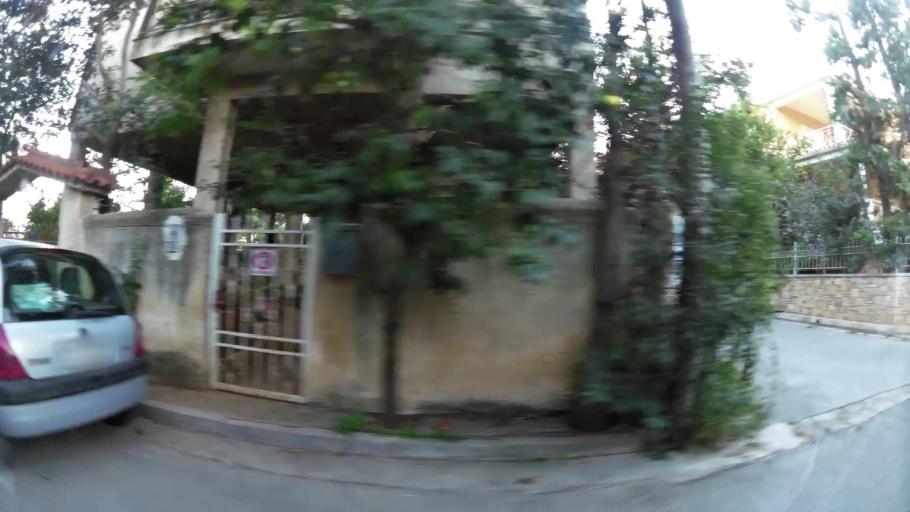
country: GR
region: Attica
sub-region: Nomarchia Anatolikis Attikis
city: Paiania
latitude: 37.9556
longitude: 23.8484
